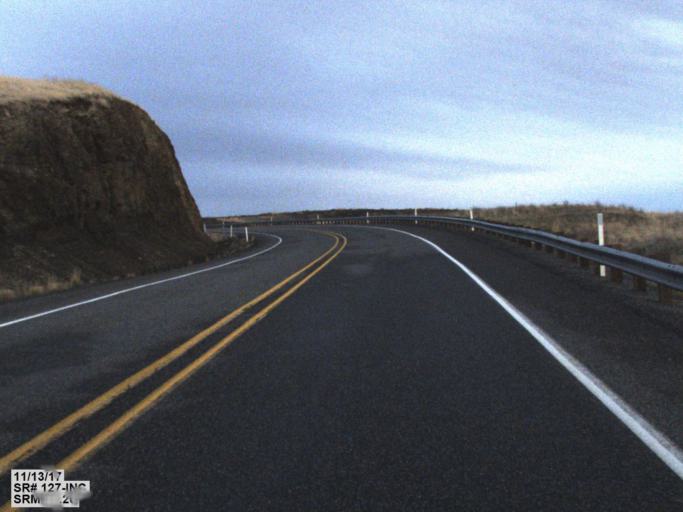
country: US
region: Washington
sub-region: Garfield County
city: Pomeroy
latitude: 46.5256
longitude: -117.7995
